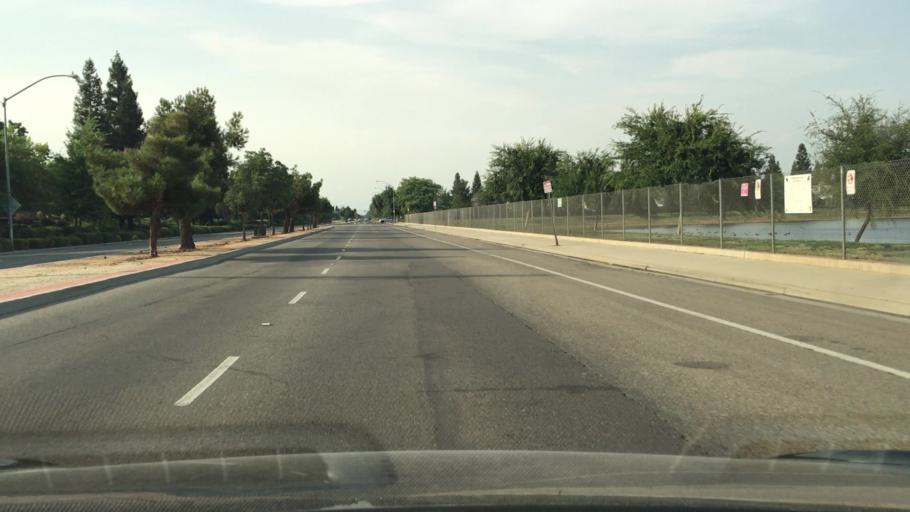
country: US
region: California
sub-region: Fresno County
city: Clovis
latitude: 36.8465
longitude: -119.7387
